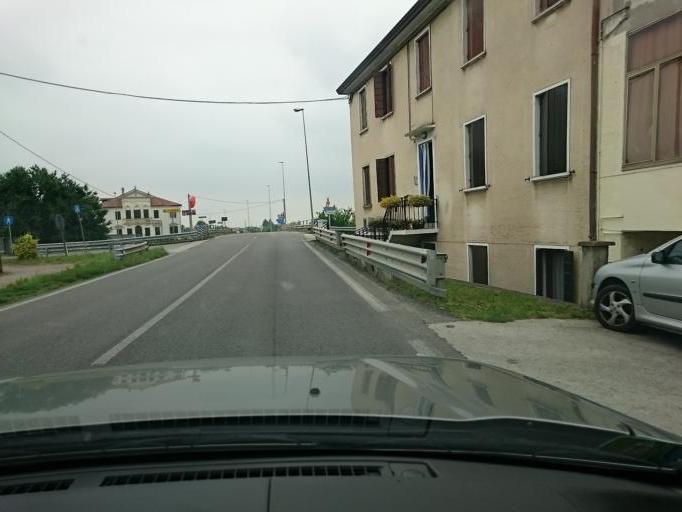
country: IT
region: Veneto
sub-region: Provincia di Padova
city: Cartura
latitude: 45.2863
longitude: 11.8706
